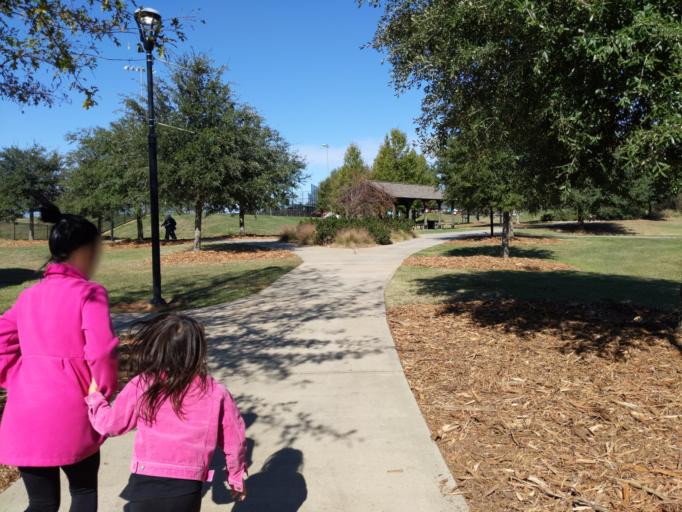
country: US
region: South Carolina
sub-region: Spartanburg County
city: Duncan
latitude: 34.8707
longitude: -82.1042
